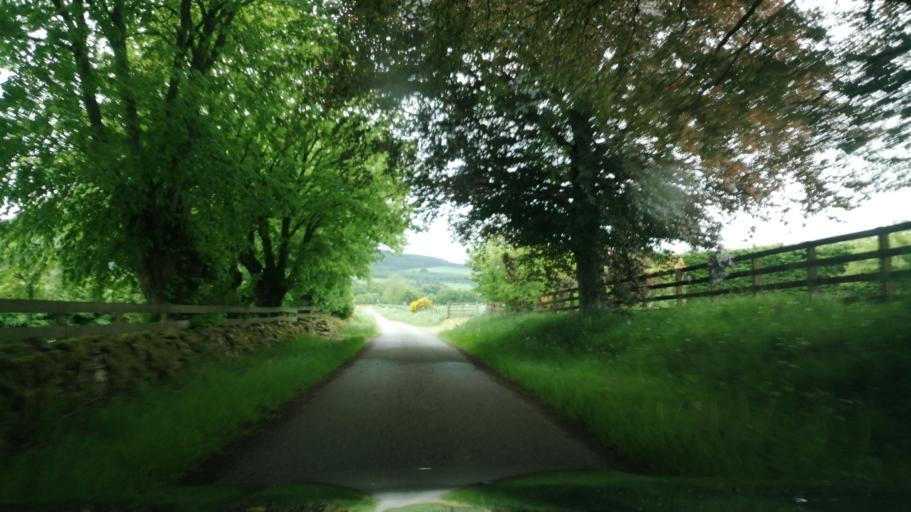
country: GB
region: Scotland
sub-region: Moray
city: Keith
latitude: 57.5566
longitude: -2.8665
